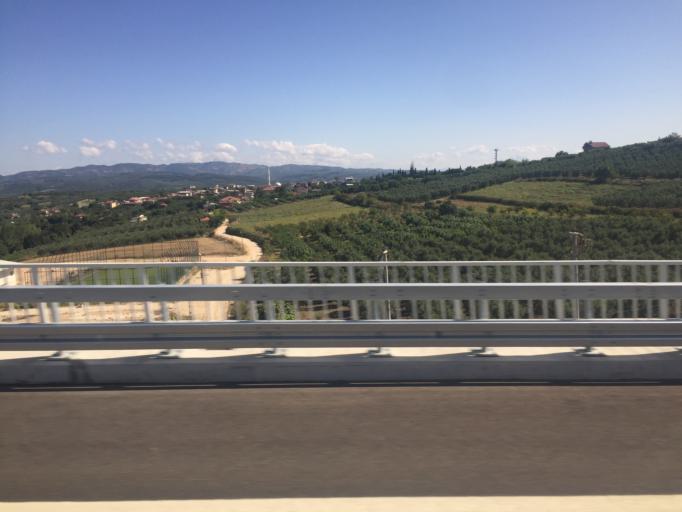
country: TR
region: Bursa
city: Gorukle
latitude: 40.2484
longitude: 28.7526
